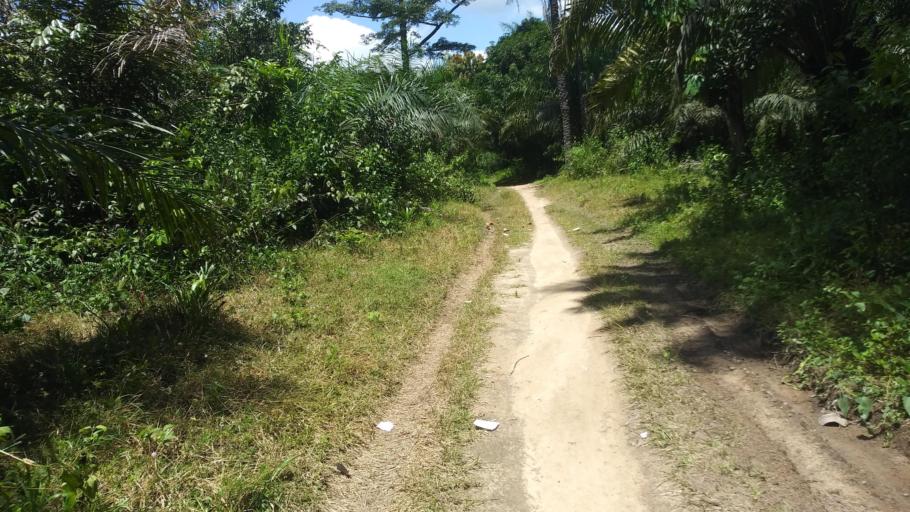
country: SL
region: Northern Province
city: Binkolo
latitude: 8.9058
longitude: -11.9770
